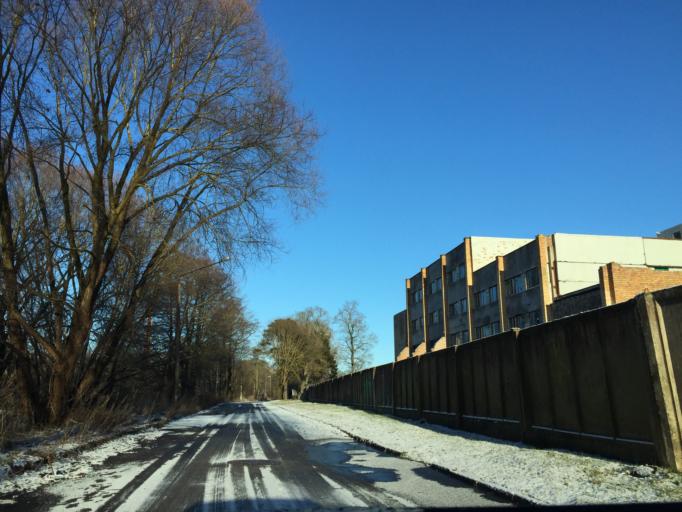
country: LV
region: Kekava
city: Balozi
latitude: 56.9092
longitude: 24.1394
